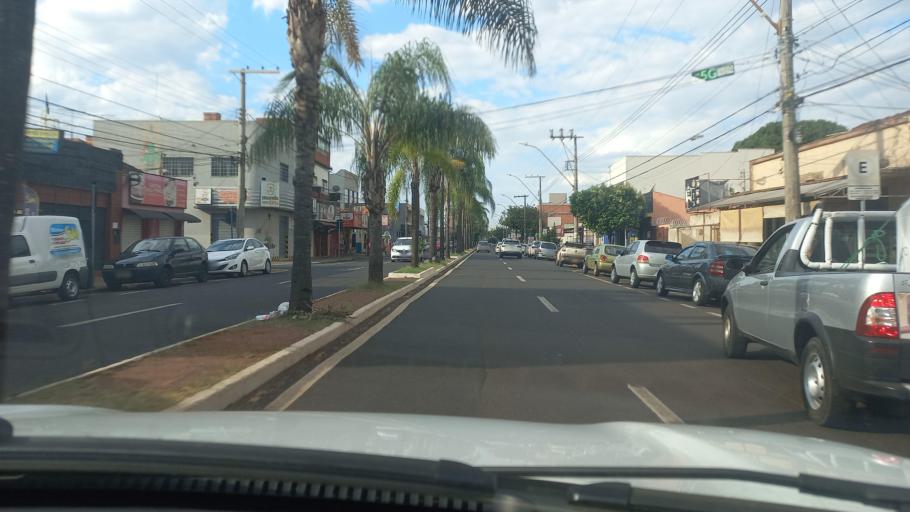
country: BR
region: Minas Gerais
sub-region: Uberaba
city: Uberaba
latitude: -19.7673
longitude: -47.9436
